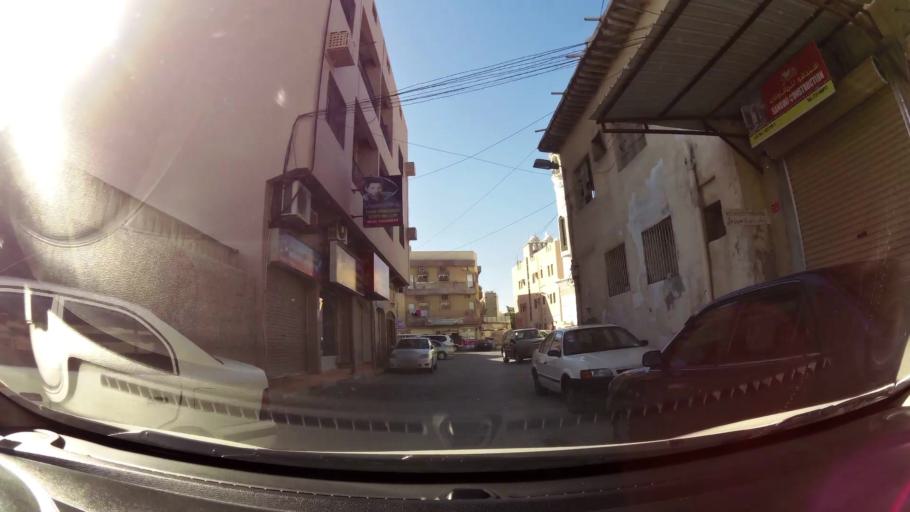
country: BH
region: Muharraq
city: Al Muharraq
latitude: 26.2584
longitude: 50.6117
